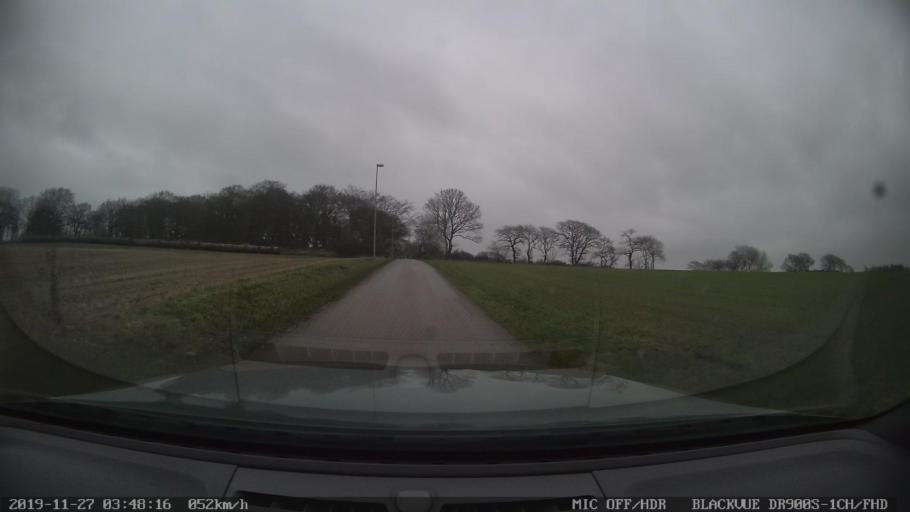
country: SE
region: Skane
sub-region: Hoganas Kommun
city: Hoganas
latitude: 56.2603
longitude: 12.5668
